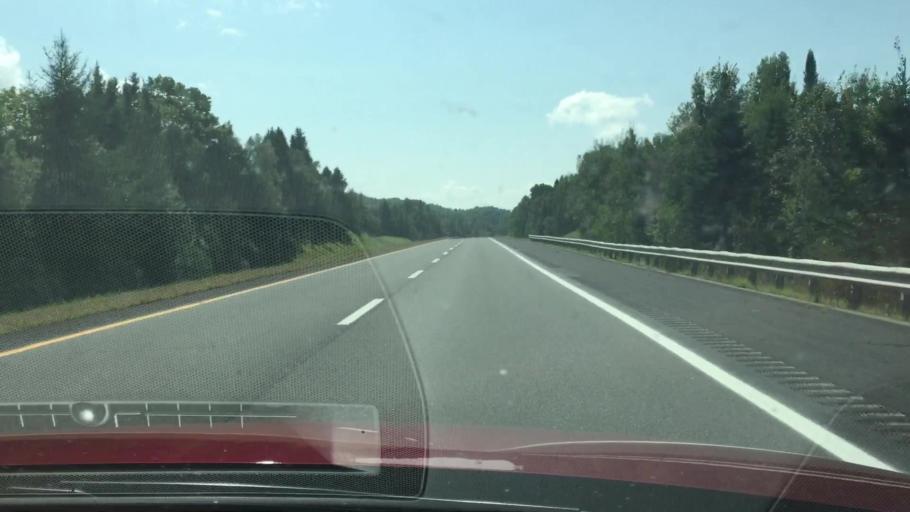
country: US
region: Maine
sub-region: Penobscot County
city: Patten
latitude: 45.9245
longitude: -68.3667
